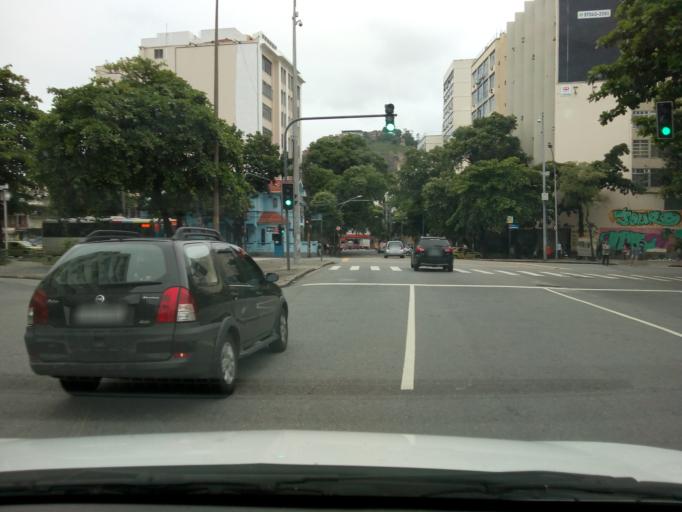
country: BR
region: Rio de Janeiro
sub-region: Rio De Janeiro
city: Rio de Janeiro
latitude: -22.9203
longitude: -43.2229
